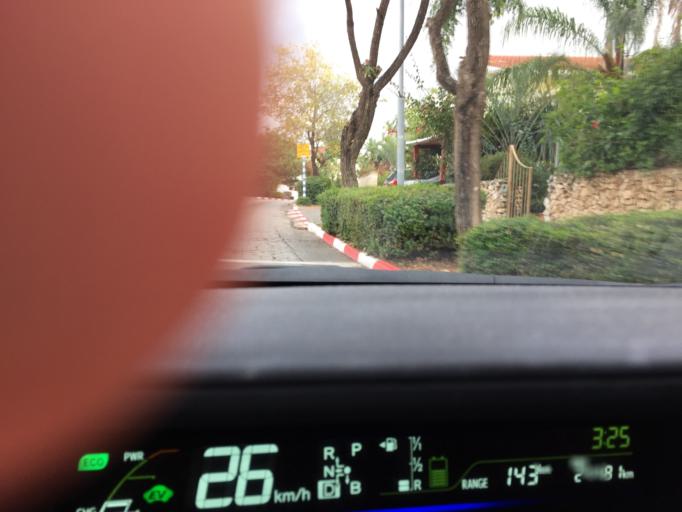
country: PS
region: West Bank
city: Mashah
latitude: 32.1094
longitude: 35.0386
